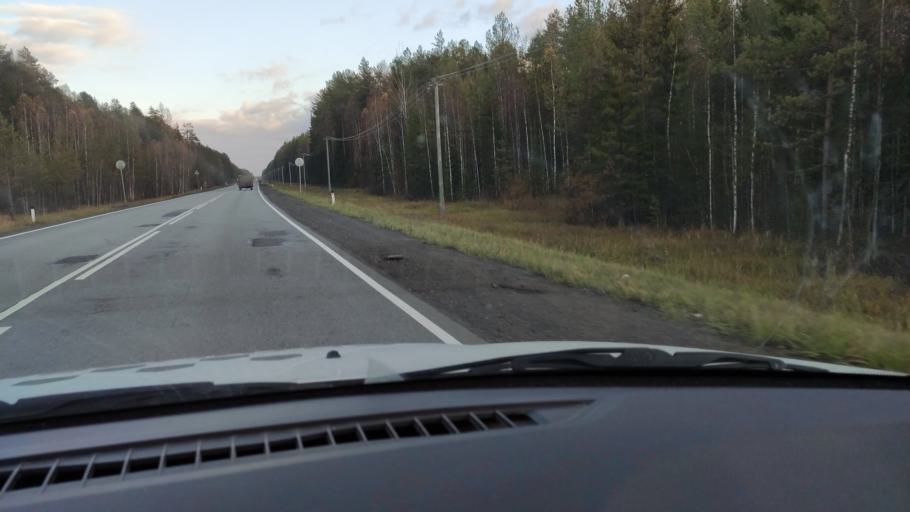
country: RU
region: Kirov
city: Belaya Kholunitsa
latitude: 58.9087
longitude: 50.9890
